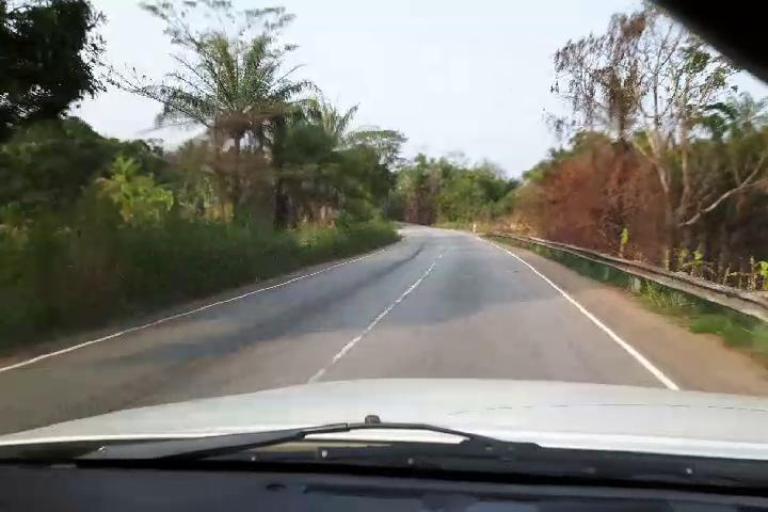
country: SL
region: Southern Province
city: Palima
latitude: 7.9290
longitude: -11.5326
